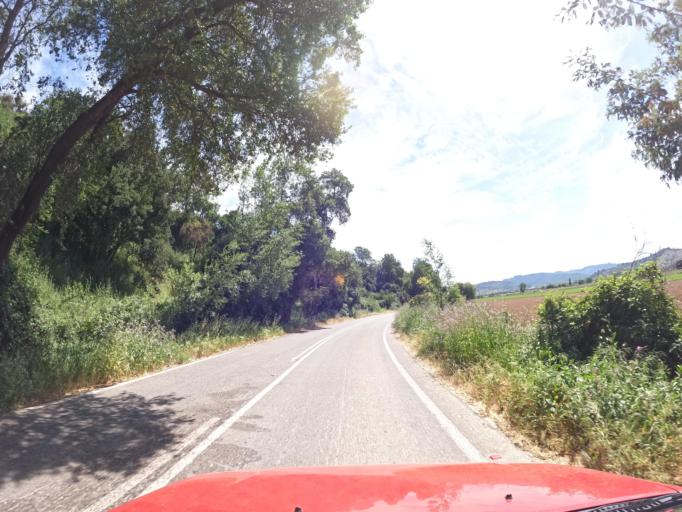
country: CL
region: Maule
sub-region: Provincia de Talca
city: Talca
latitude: -34.9897
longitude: -71.8232
